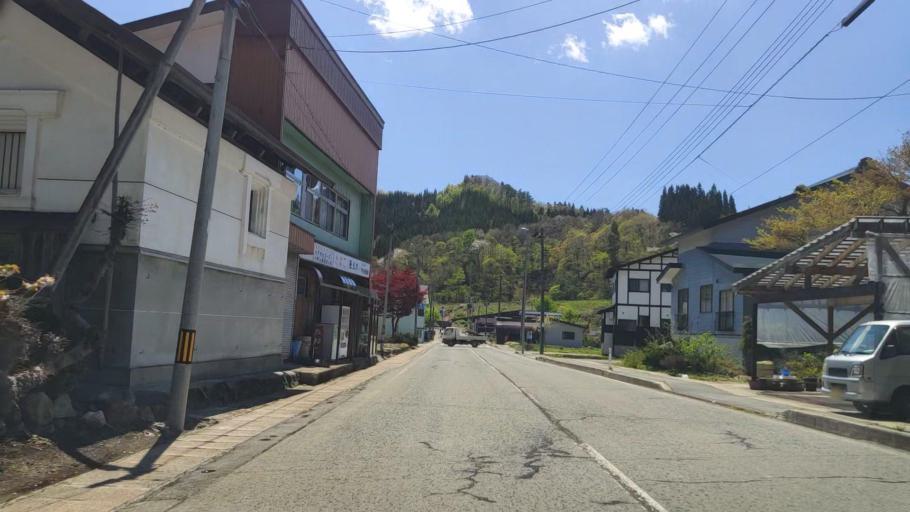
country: JP
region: Yamagata
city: Shinjo
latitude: 38.9223
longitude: 140.3337
